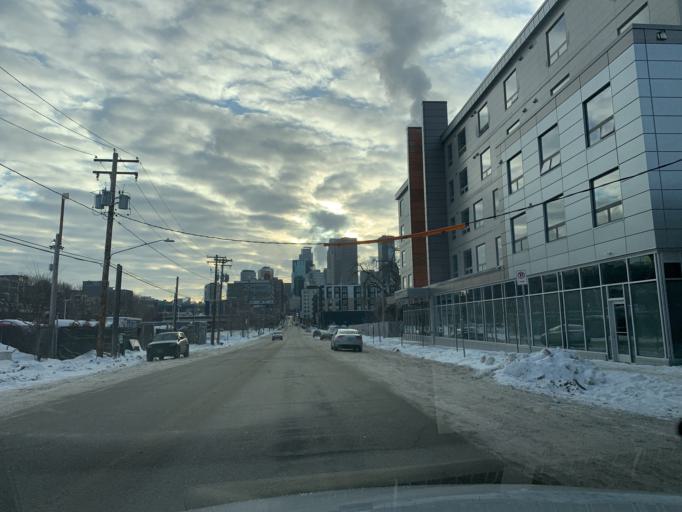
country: US
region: Minnesota
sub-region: Hennepin County
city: Minneapolis
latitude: 44.9874
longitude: -93.2834
